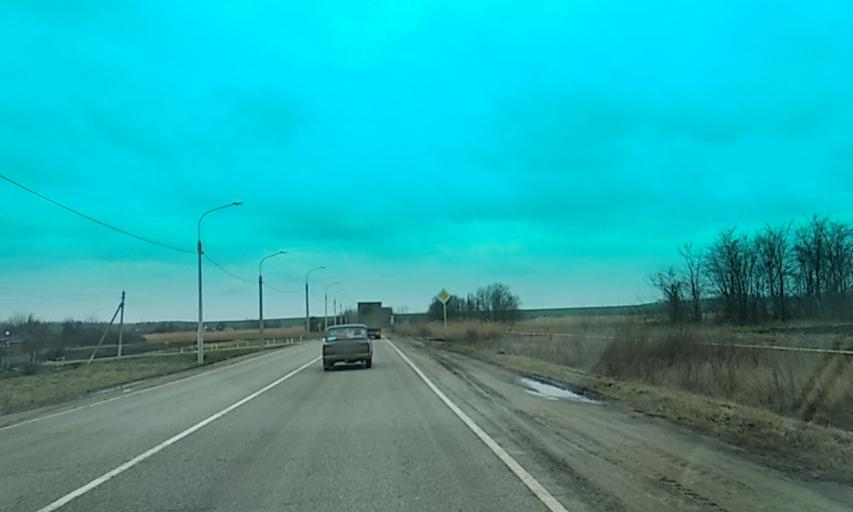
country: RU
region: Krasnodarskiy
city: Vyselki
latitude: 45.4840
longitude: 39.7079
